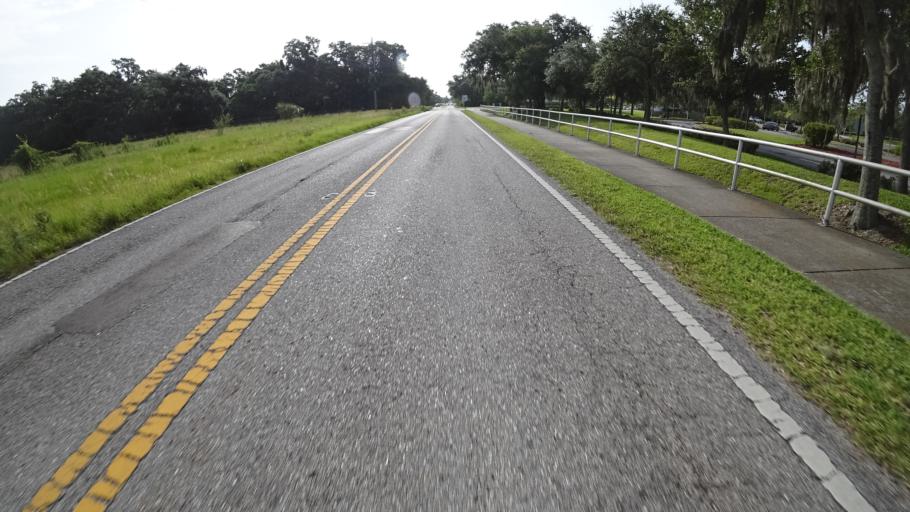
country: US
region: Florida
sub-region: Manatee County
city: Ellenton
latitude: 27.5469
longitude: -82.5065
